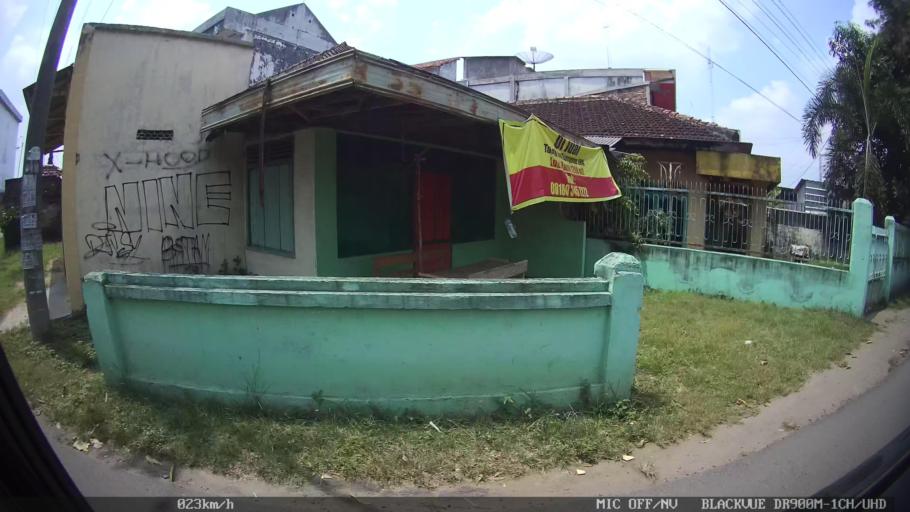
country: ID
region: Lampung
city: Pringsewu
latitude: -5.3536
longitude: 104.9731
